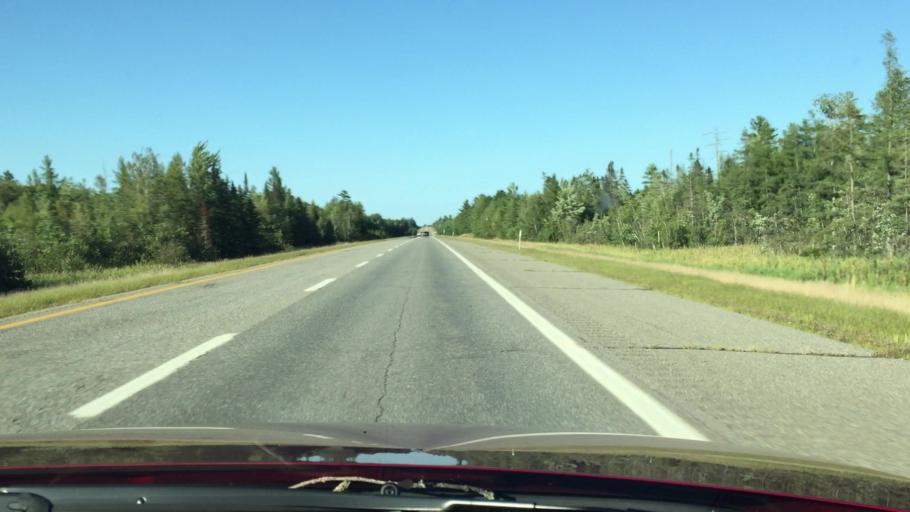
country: US
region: Maine
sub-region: Penobscot County
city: Howland
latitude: 45.3303
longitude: -68.6358
